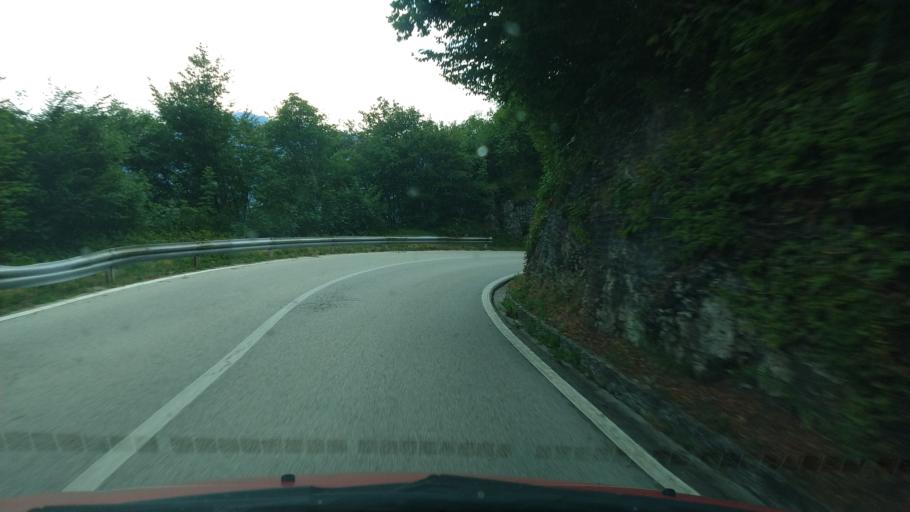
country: IT
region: Veneto
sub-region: Provincia di Vicenza
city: Arsiero
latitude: 45.8244
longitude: 11.3637
